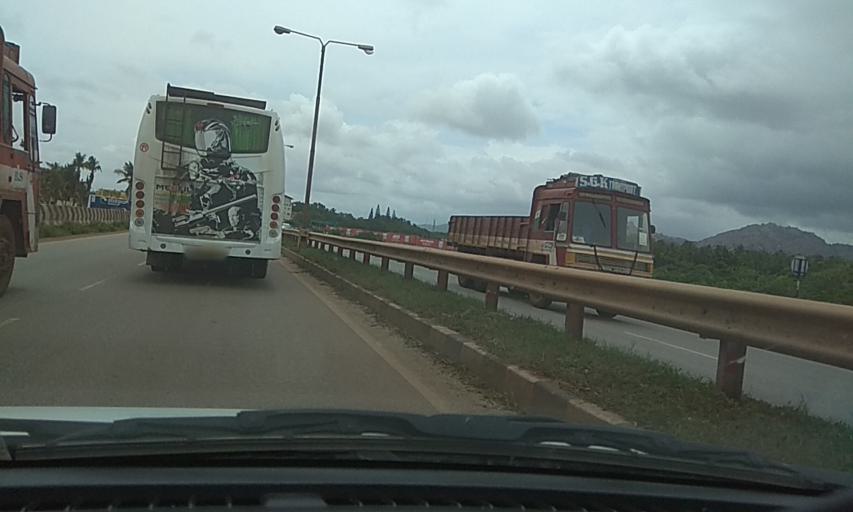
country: IN
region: Karnataka
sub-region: Chitradurga
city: Chitradurga
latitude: 14.2375
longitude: 76.3809
